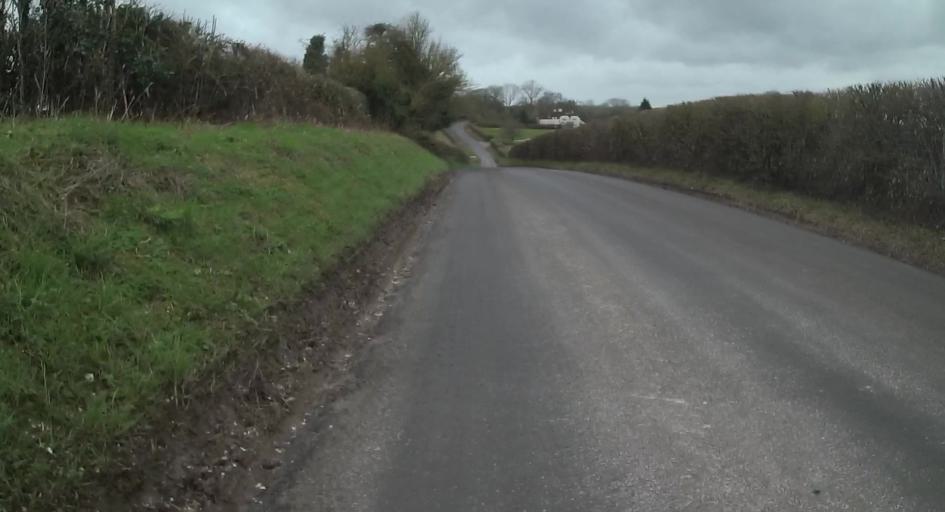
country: GB
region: England
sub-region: Hampshire
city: Kingsclere
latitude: 51.3290
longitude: -1.2757
